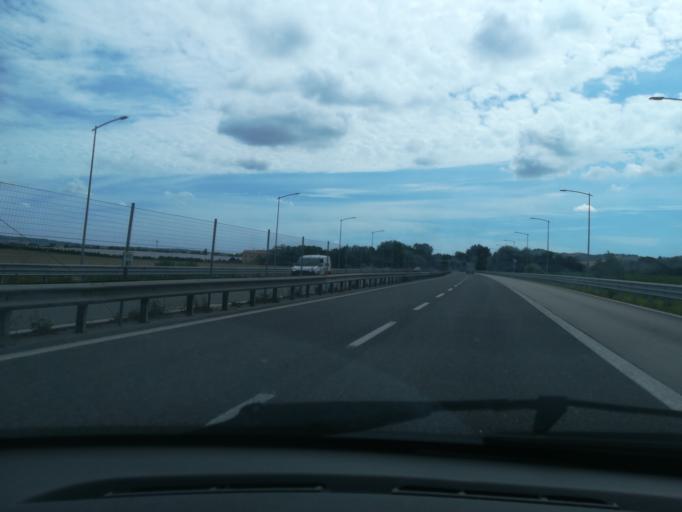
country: IT
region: The Marches
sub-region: Provincia di Macerata
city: Villa San Filippo
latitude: 43.2624
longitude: 13.5641
